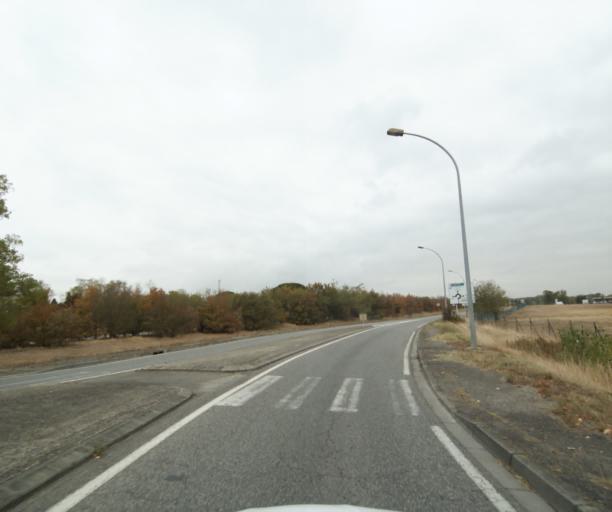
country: FR
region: Midi-Pyrenees
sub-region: Departement de la Haute-Garonne
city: Villefranche-de-Lauragais
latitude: 43.4015
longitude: 1.7007
